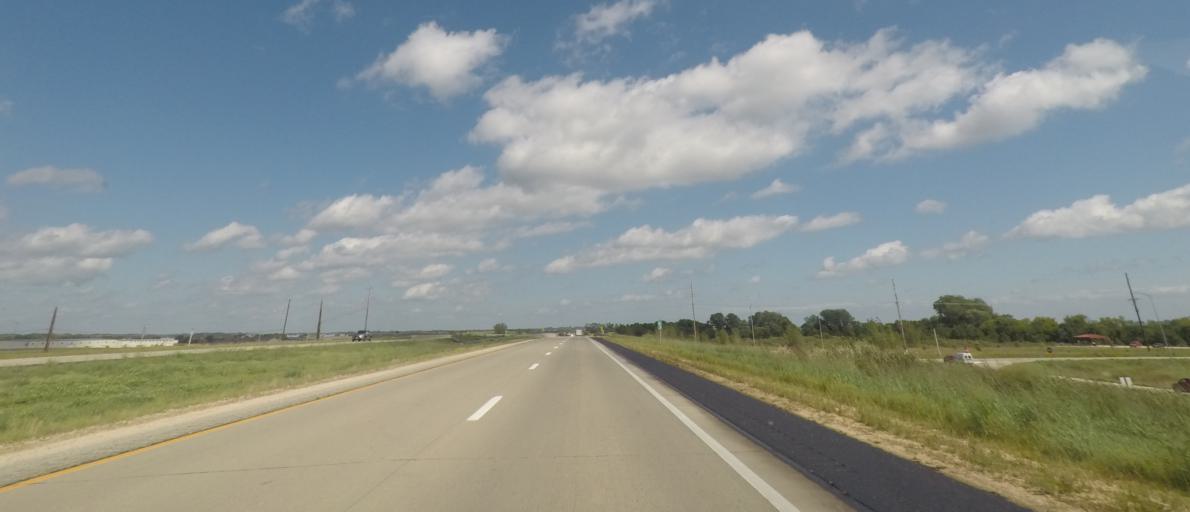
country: US
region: Iowa
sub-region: Jones County
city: Monticello
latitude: 42.2070
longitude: -91.1916
